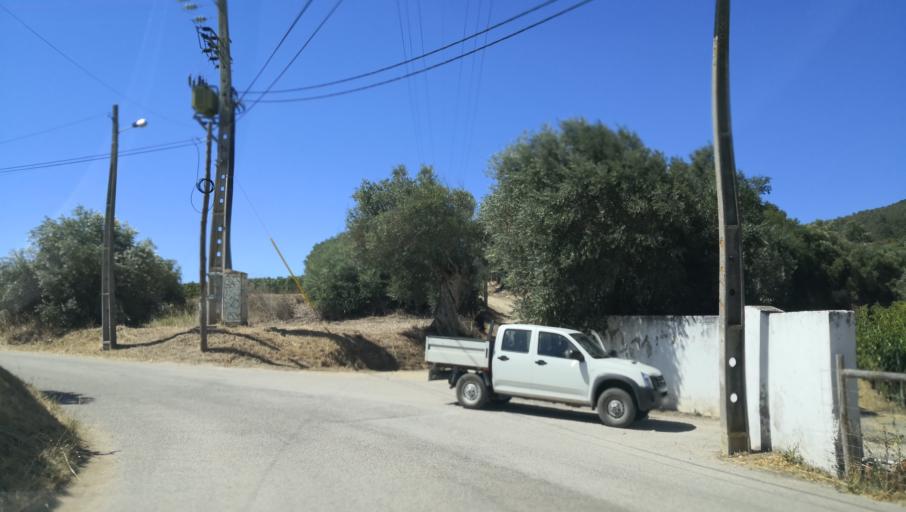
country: PT
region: Setubal
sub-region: Setubal
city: Setubal
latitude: 38.5361
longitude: -8.9149
